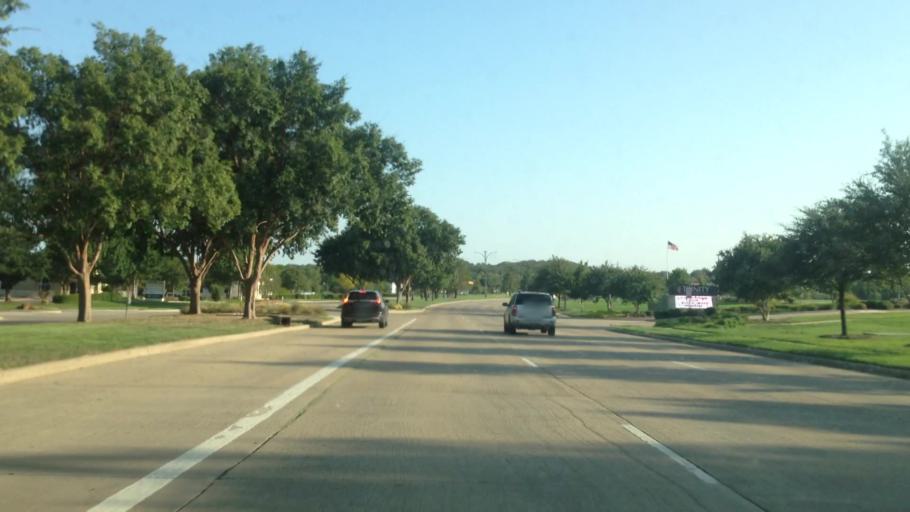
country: US
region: Texas
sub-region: Tarrant County
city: Pantego
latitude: 32.7267
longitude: -97.1813
